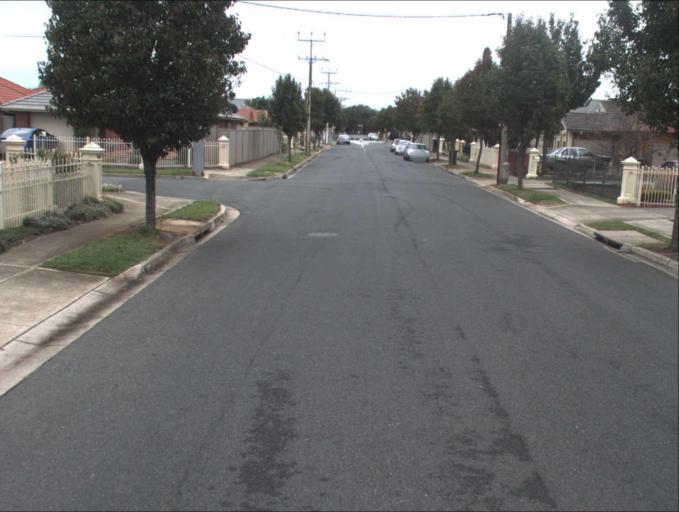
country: AU
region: South Australia
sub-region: Charles Sturt
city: Woodville North
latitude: -34.8676
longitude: 138.5562
